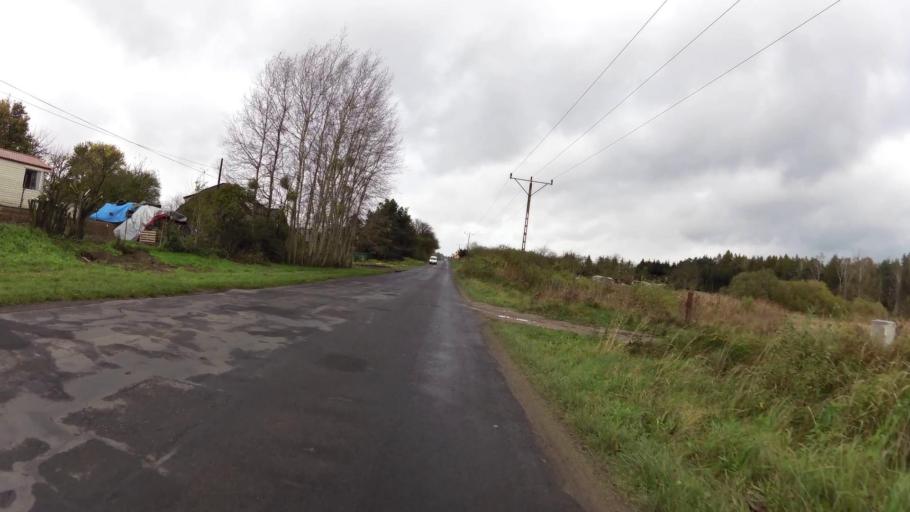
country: PL
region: West Pomeranian Voivodeship
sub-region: Powiat gryfinski
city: Gryfino
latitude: 53.2395
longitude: 14.5101
